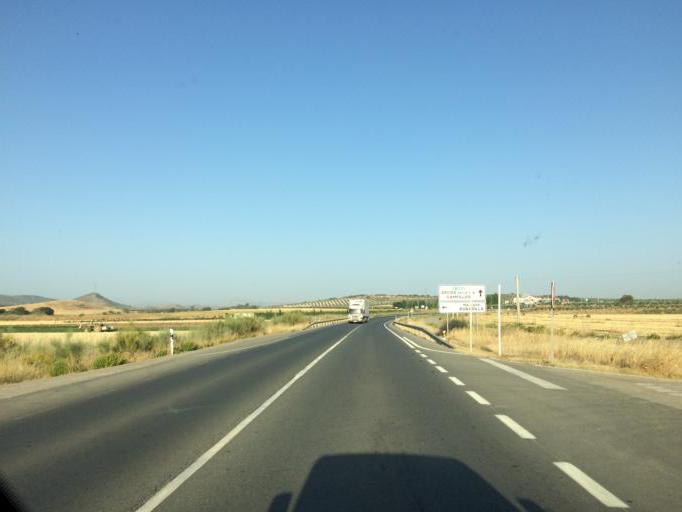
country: ES
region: Andalusia
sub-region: Provincia de Malaga
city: Mollina
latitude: 37.0514
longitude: -4.6502
